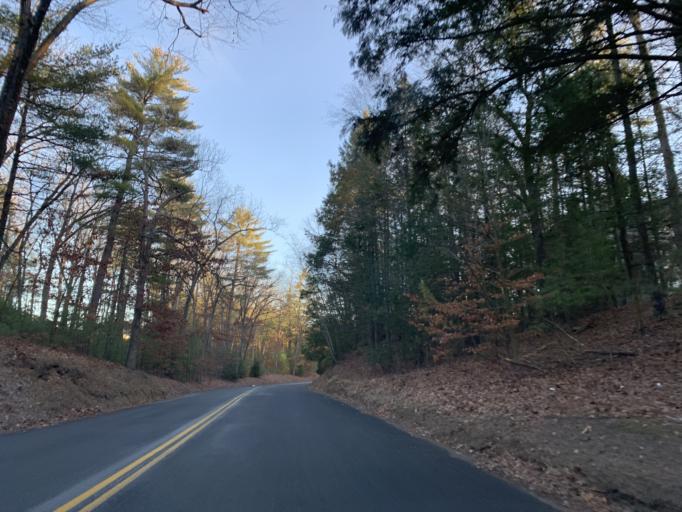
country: US
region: Connecticut
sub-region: Hartford County
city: Weatogue
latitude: 41.8537
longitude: -72.8223
